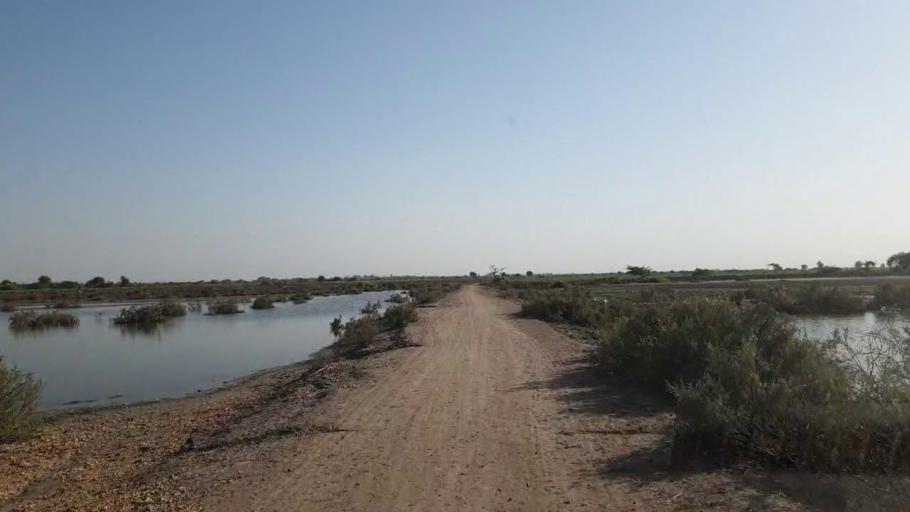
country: PK
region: Sindh
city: Badin
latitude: 24.5911
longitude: 68.9129
